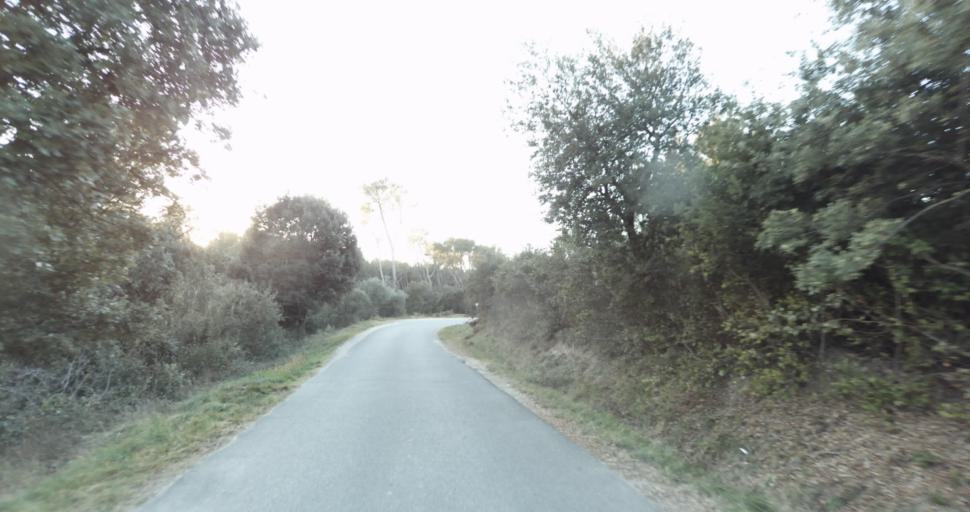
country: FR
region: Provence-Alpes-Cote d'Azur
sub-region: Departement des Bouches-du-Rhone
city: Barbentane
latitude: 43.8839
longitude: 4.7610
